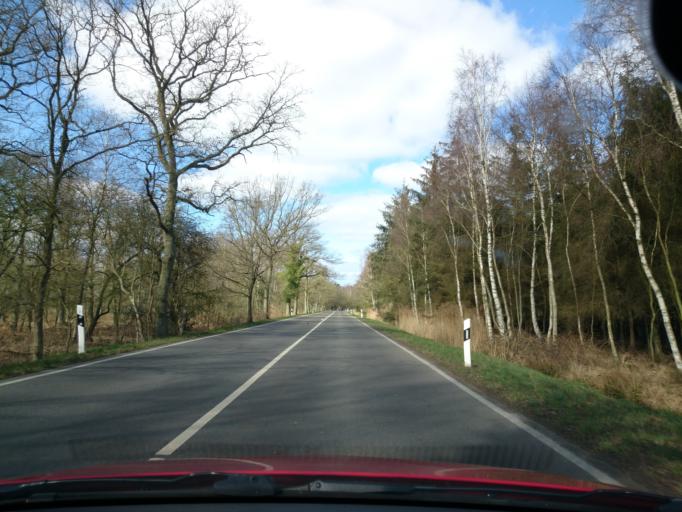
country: DE
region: Mecklenburg-Vorpommern
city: Zingst
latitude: 54.4195
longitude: 12.6557
